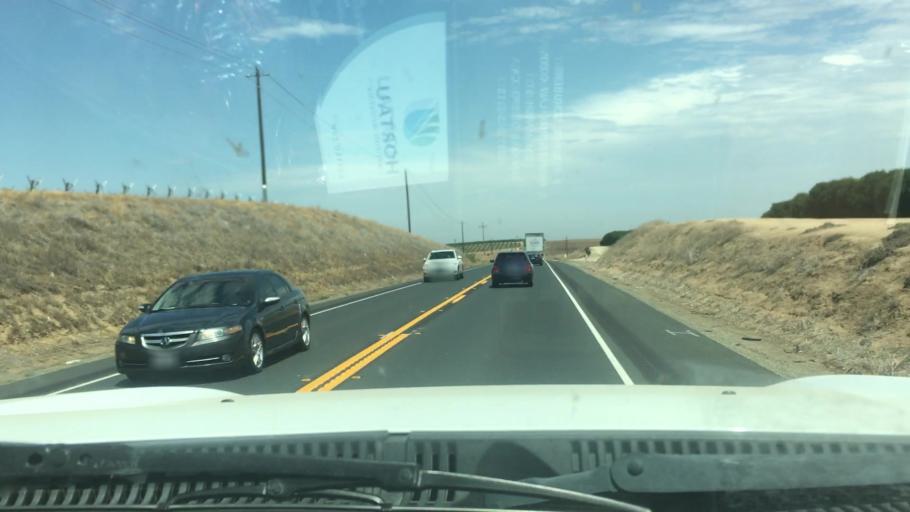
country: US
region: California
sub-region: Tulare County
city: Richgrove
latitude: 35.7869
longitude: -119.0534
